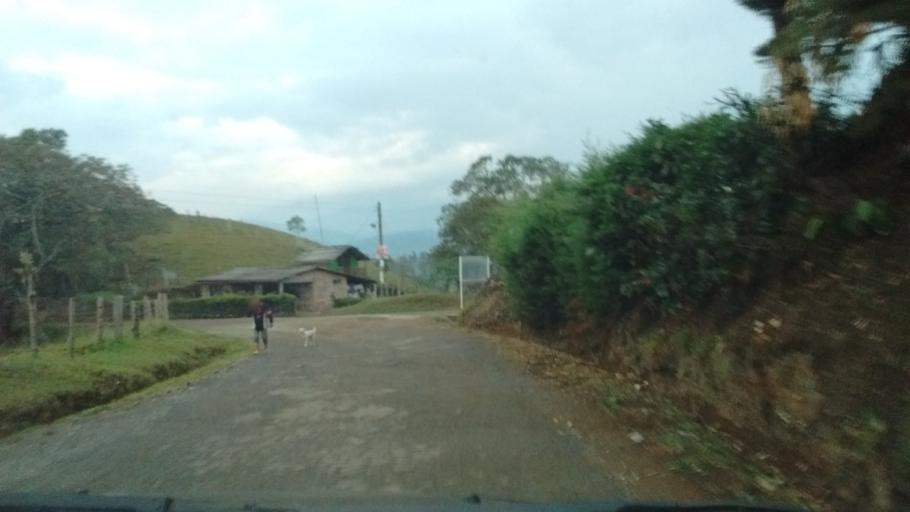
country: CO
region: Cauca
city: Lopez
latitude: 2.3781
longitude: -76.7171
